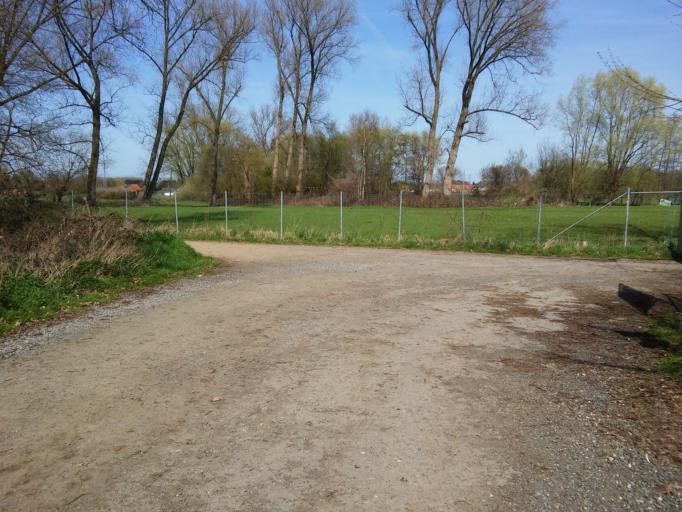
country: BE
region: Flanders
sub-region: Provincie Antwerpen
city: Rumst
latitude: 51.0929
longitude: 4.4018
